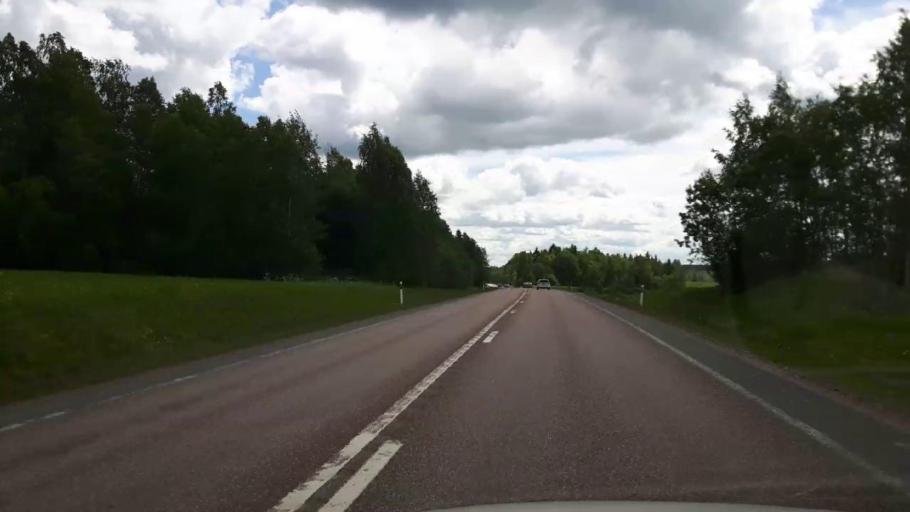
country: SE
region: Dalarna
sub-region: Saters Kommun
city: Saeter
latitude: 60.4833
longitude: 15.7720
